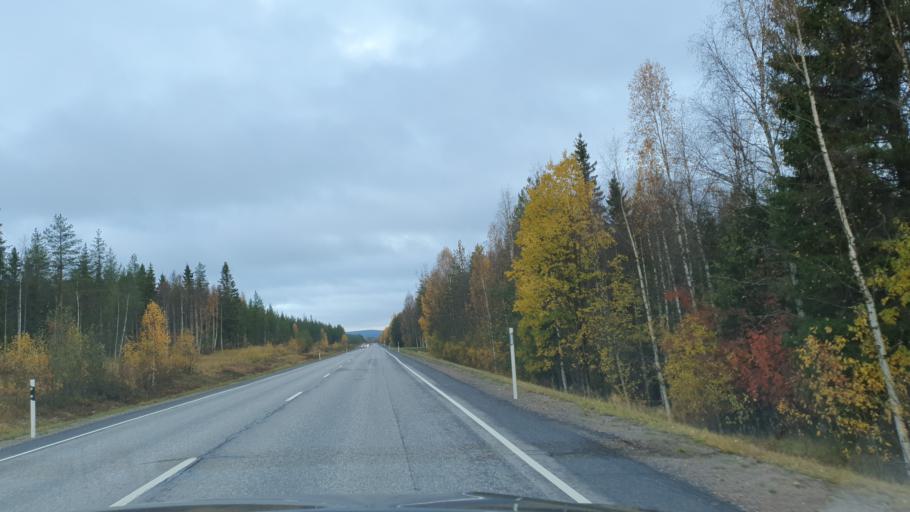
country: FI
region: Lapland
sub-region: Rovaniemi
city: Rovaniemi
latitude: 66.5567
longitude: 25.6478
